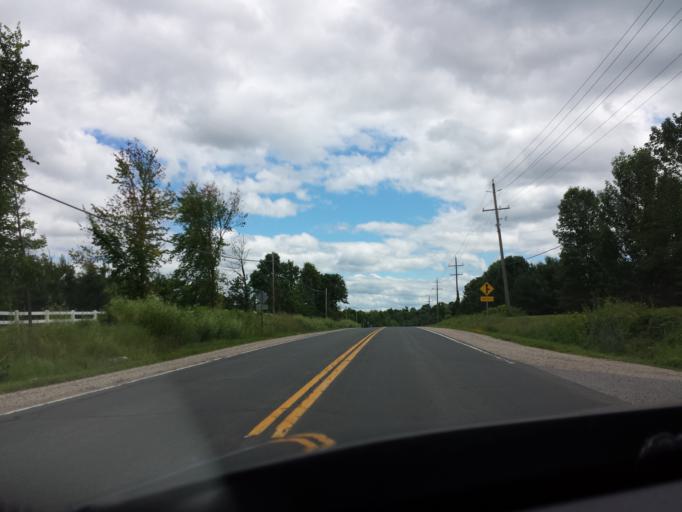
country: CA
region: Ontario
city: Perth
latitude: 44.8717
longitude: -76.2003
